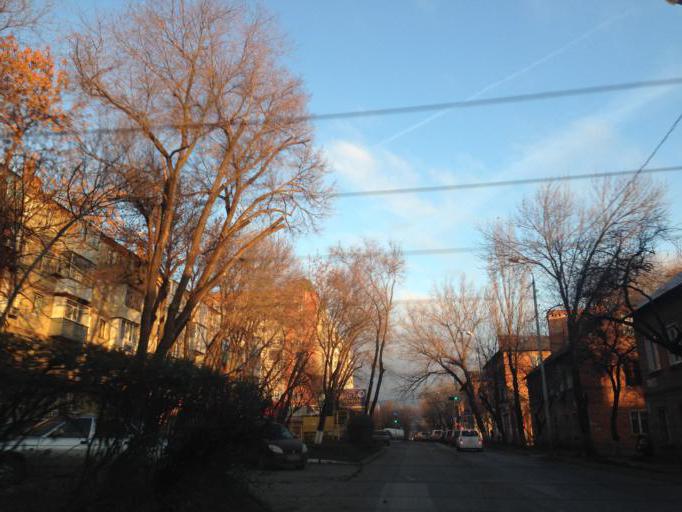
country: RU
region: Rostov
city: Rostov-na-Donu
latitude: 47.2503
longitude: 39.6870
